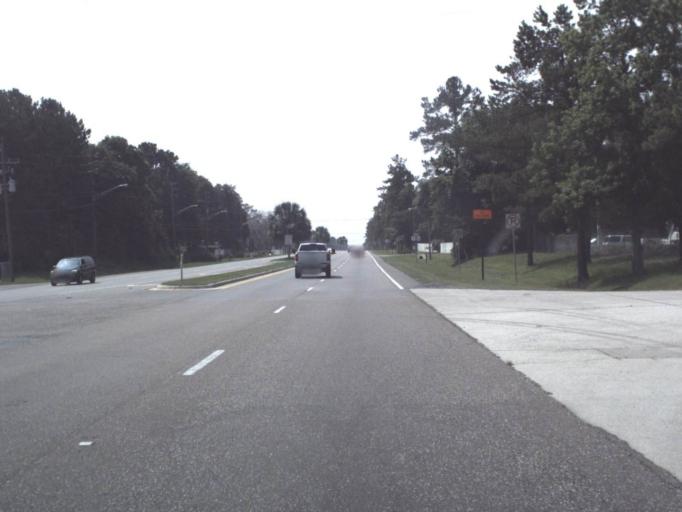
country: US
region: Florida
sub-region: Duval County
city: Jacksonville
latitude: 30.4091
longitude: -81.7458
